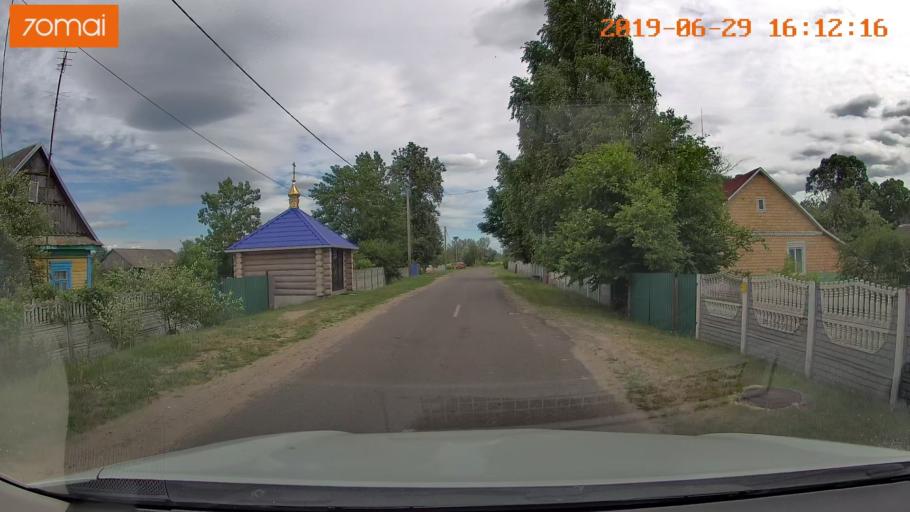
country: BY
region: Brest
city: Luninyets
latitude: 52.2012
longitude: 27.0139
